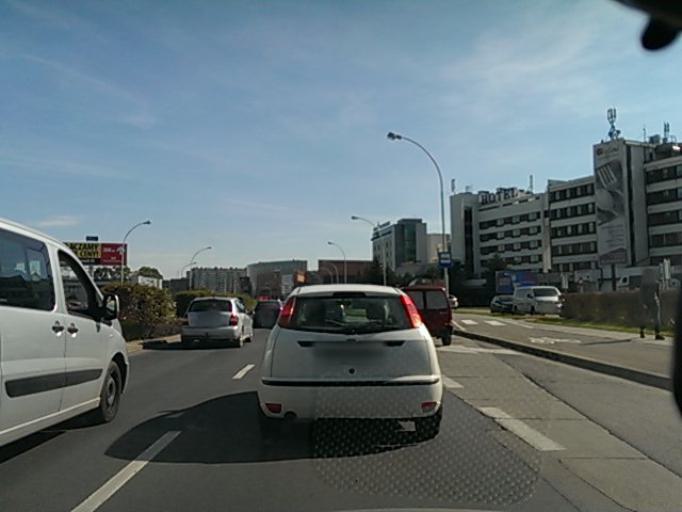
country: PL
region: Subcarpathian Voivodeship
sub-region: Rzeszow
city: Rzeszow
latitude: 50.0292
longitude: 22.0086
